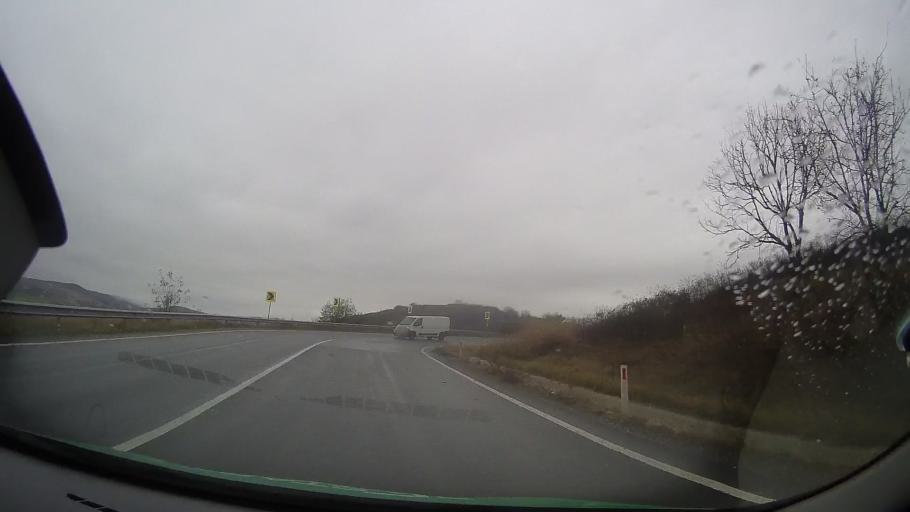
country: RO
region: Bistrita-Nasaud
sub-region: Comuna Teaca
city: Teaca
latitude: 46.9014
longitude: 24.5067
